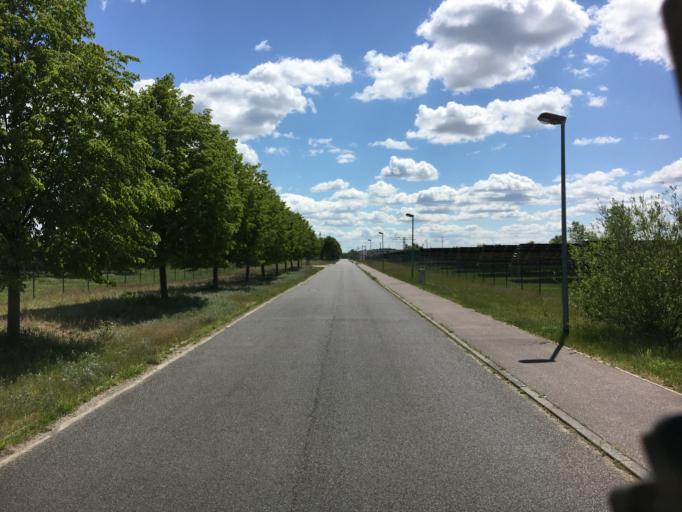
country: DE
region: Brandenburg
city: Trebbin
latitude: 52.1901
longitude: 13.2375
